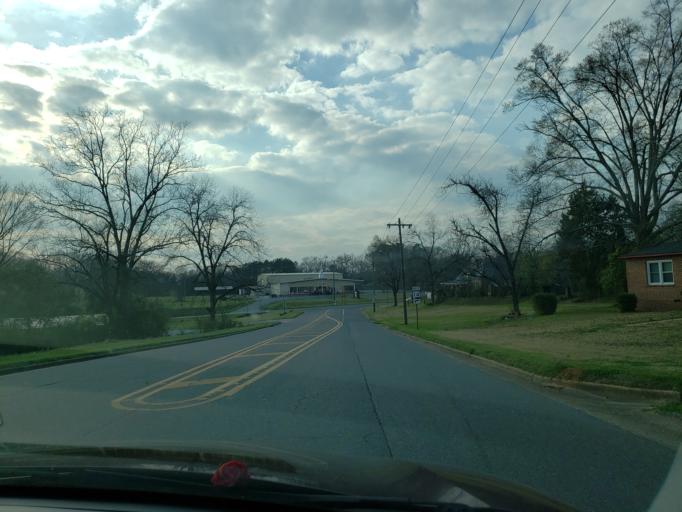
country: US
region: Alabama
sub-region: Hale County
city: Greensboro
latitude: 32.7011
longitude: -87.6055
